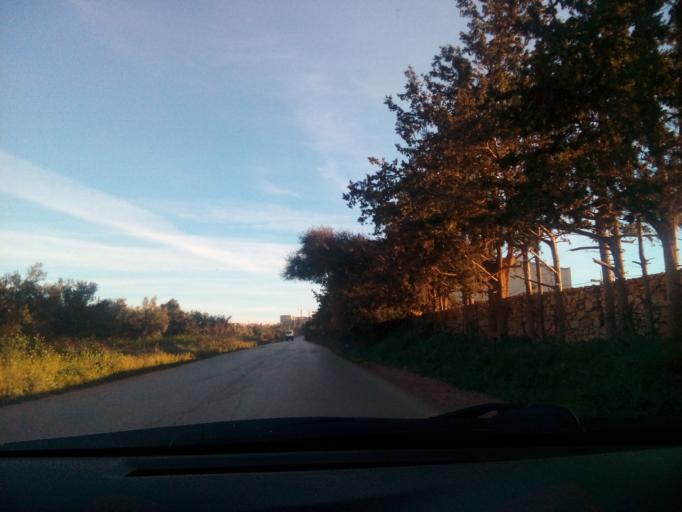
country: DZ
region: Oran
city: Es Senia
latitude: 35.6202
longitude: -0.6814
